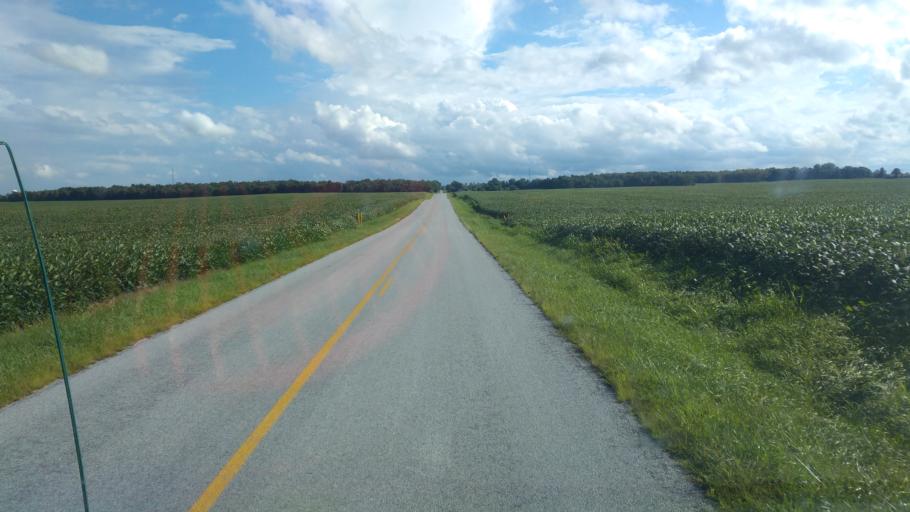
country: US
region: Ohio
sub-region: Hardin County
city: Kenton
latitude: 40.6801
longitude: -83.6335
